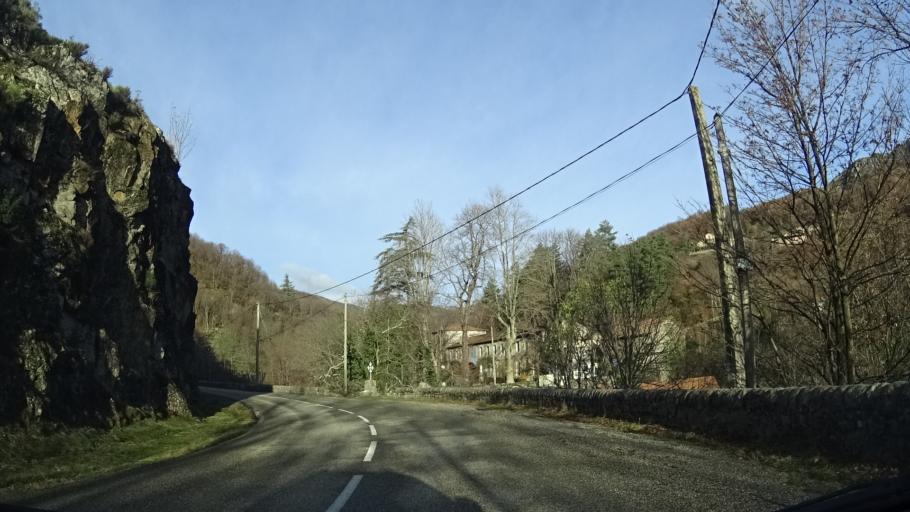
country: FR
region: Rhone-Alpes
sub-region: Departement de l'Ardeche
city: Thueyts
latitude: 44.7244
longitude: 4.2618
